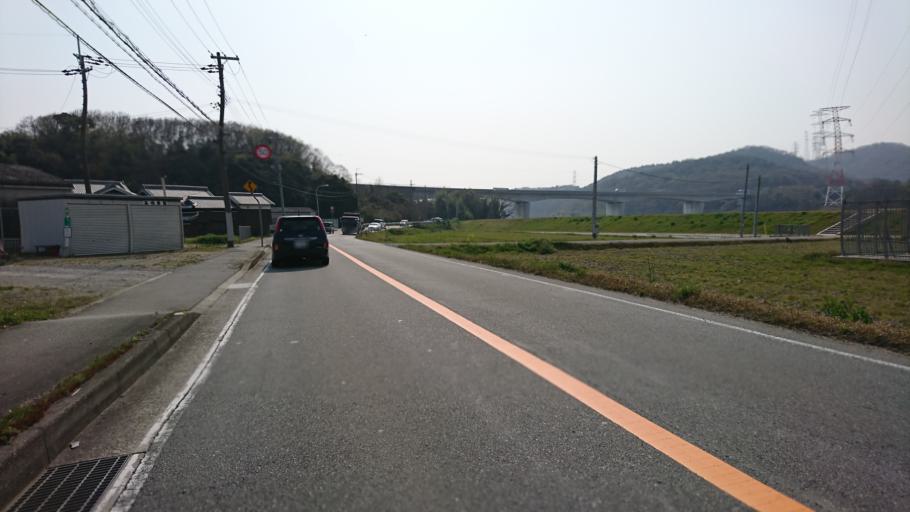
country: JP
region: Hyogo
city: Ono
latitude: 34.8128
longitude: 134.9347
